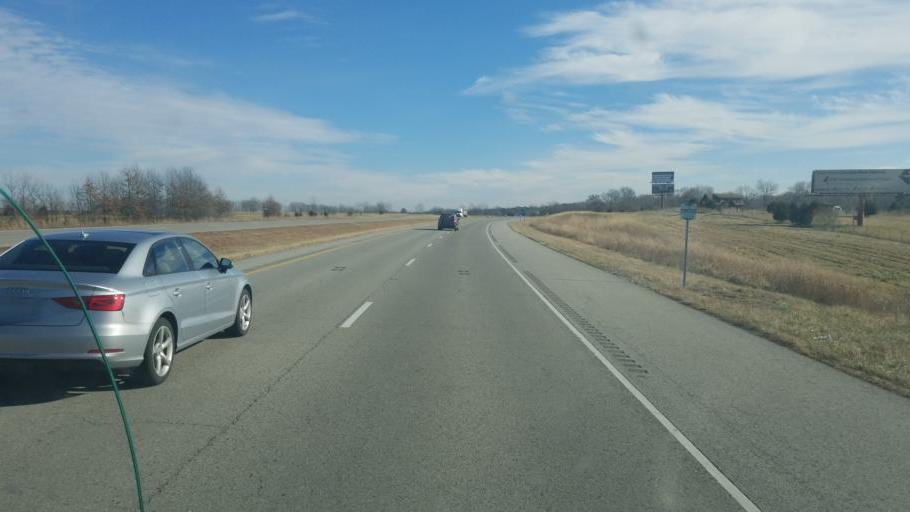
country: US
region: Illinois
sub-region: Williamson County
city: Marion
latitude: 37.7324
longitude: -88.7926
